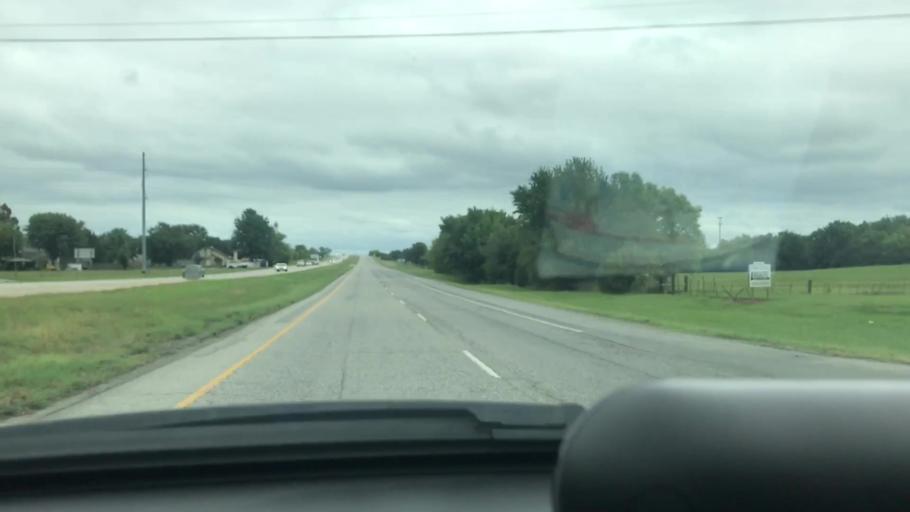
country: US
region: Oklahoma
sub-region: Wagoner County
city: Wagoner
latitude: 35.9719
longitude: -95.3867
